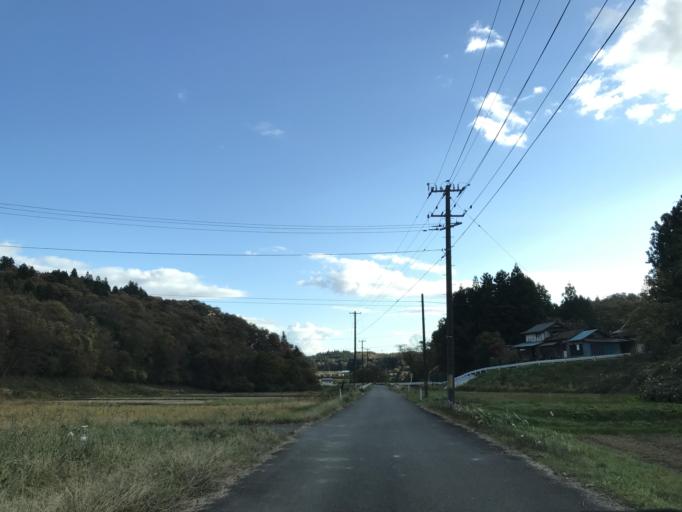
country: JP
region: Iwate
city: Ichinoseki
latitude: 38.8659
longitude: 141.1380
